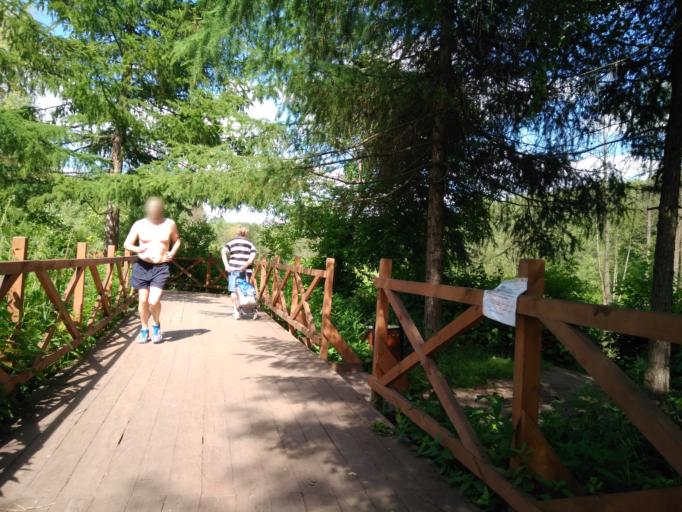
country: RU
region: Moscow
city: Pokrovskoye-Streshnevo
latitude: 55.8254
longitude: 37.4653
